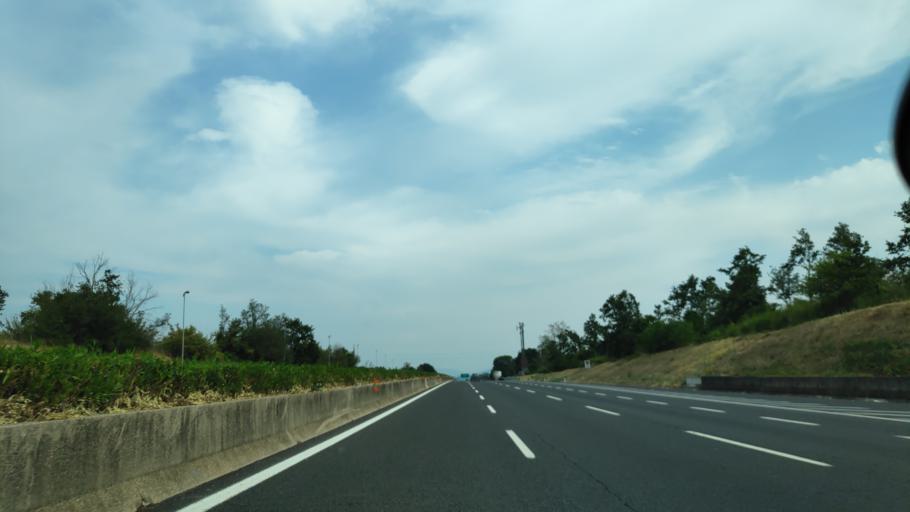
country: IT
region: Latium
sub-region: Citta metropolitana di Roma Capitale
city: Fiano Romano
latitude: 42.1723
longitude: 12.6092
